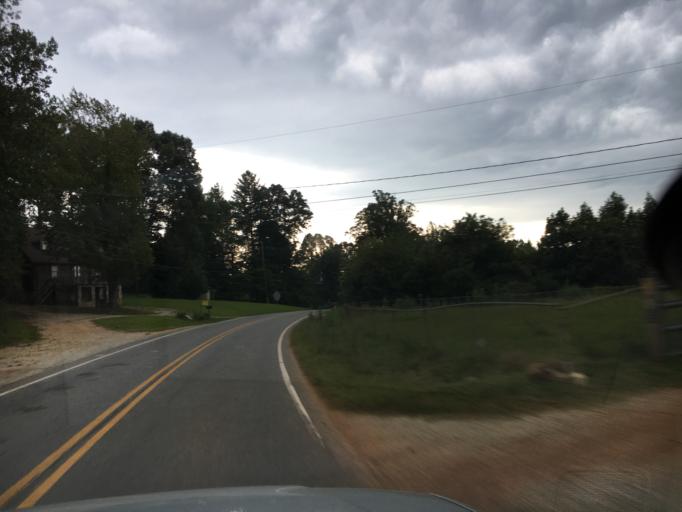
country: US
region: North Carolina
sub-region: McDowell County
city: Marion
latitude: 35.7011
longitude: -81.9135
